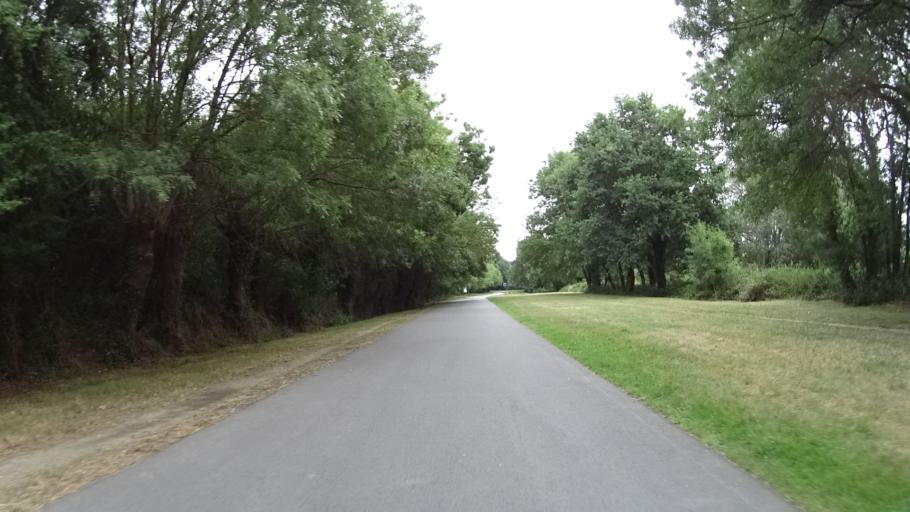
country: FR
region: Pays de la Loire
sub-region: Departement de la Loire-Atlantique
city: Thouare-sur-Loire
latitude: 47.2502
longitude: -1.4504
